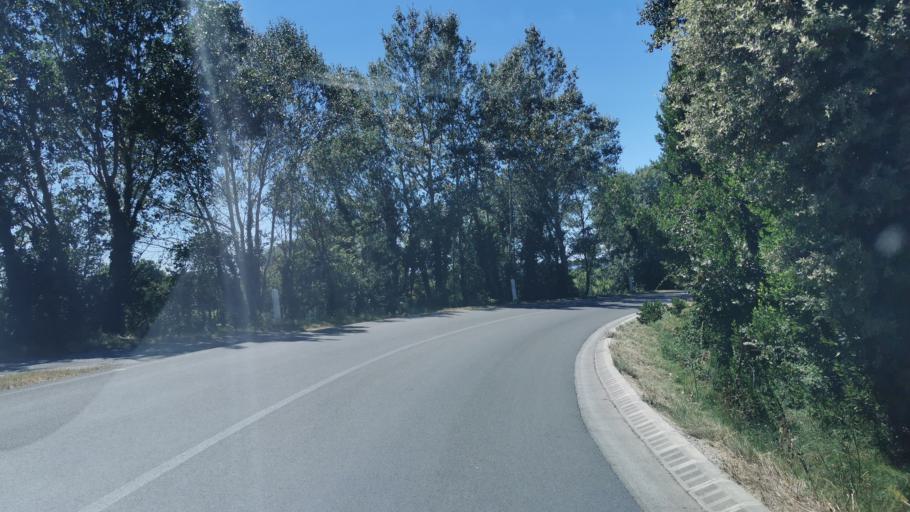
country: FR
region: Languedoc-Roussillon
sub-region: Departement de l'Aude
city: Vinassan
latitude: 43.2303
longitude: 3.0943
